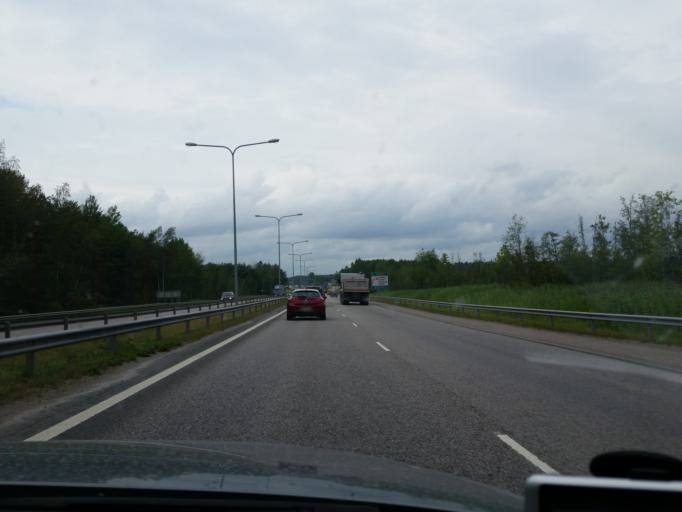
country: FI
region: Uusimaa
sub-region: Helsinki
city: Espoo
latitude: 60.2116
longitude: 24.6757
